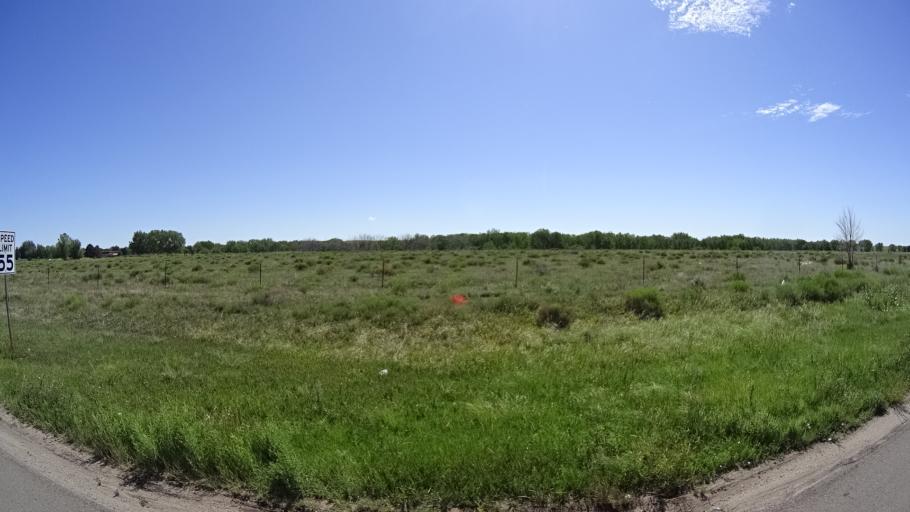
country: US
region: Colorado
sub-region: El Paso County
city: Security-Widefield
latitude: 38.7598
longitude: -104.6595
